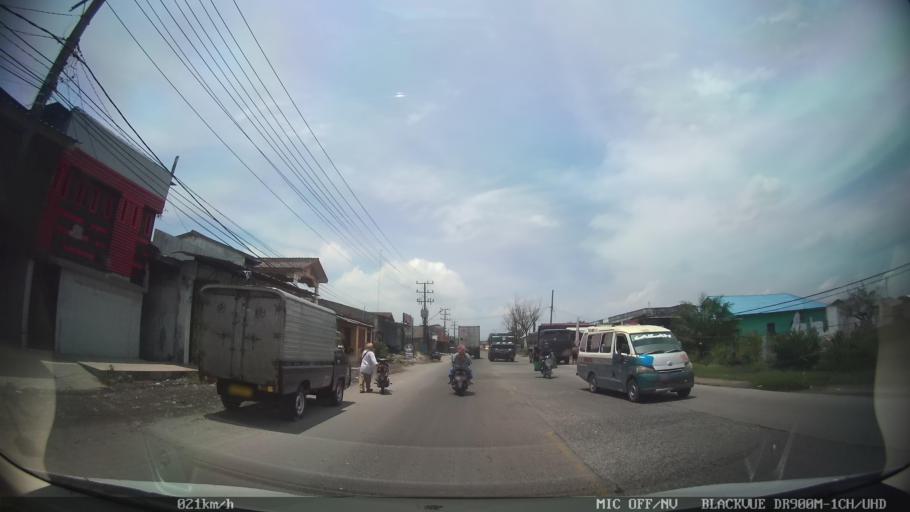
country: ID
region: North Sumatra
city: Belawan
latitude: 3.7609
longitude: 98.6810
